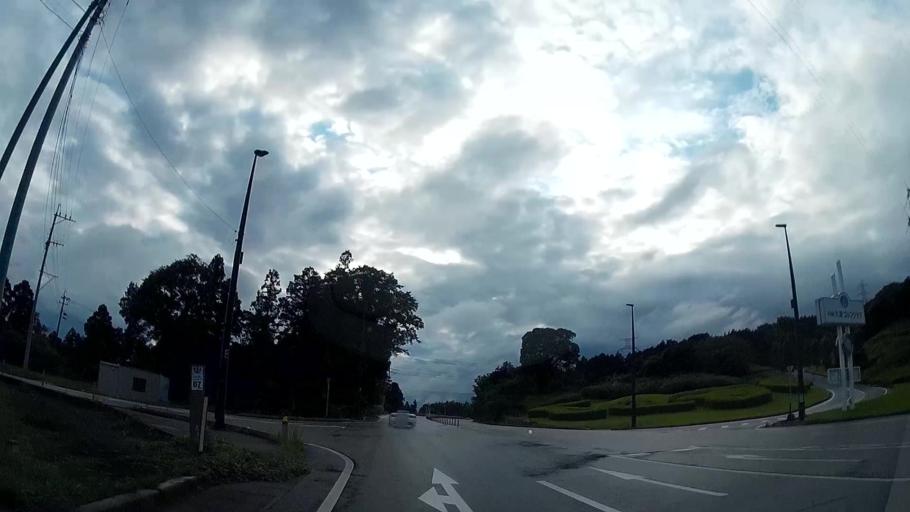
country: JP
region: Kumamoto
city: Ozu
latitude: 32.8759
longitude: 130.9282
